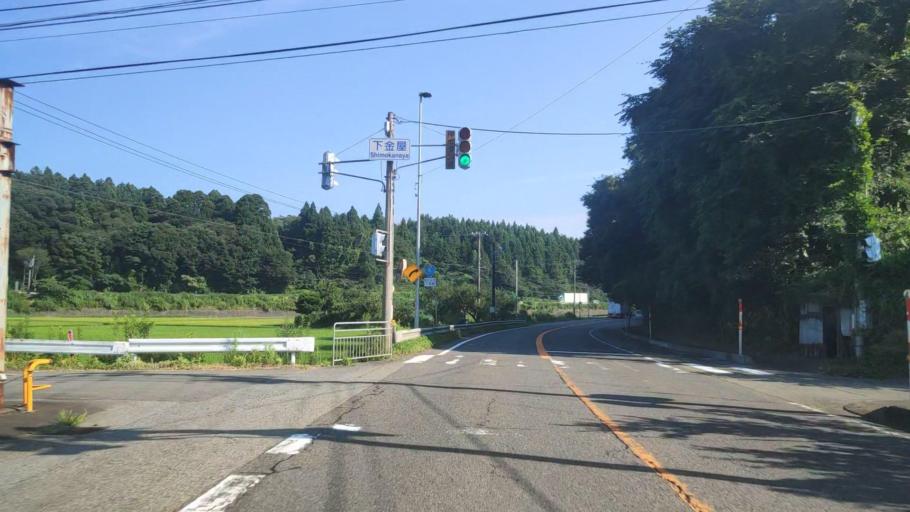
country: JP
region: Fukui
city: Maruoka
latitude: 36.2414
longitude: 136.2845
